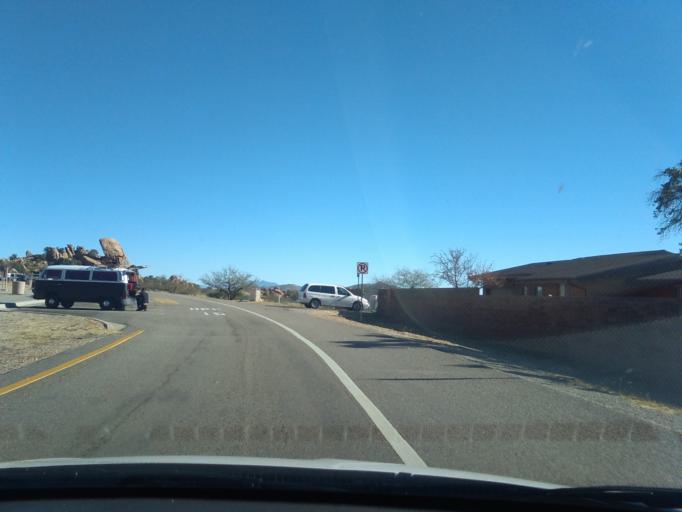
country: US
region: Arizona
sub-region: Cochise County
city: Saint David
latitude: 32.0590
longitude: -110.0768
